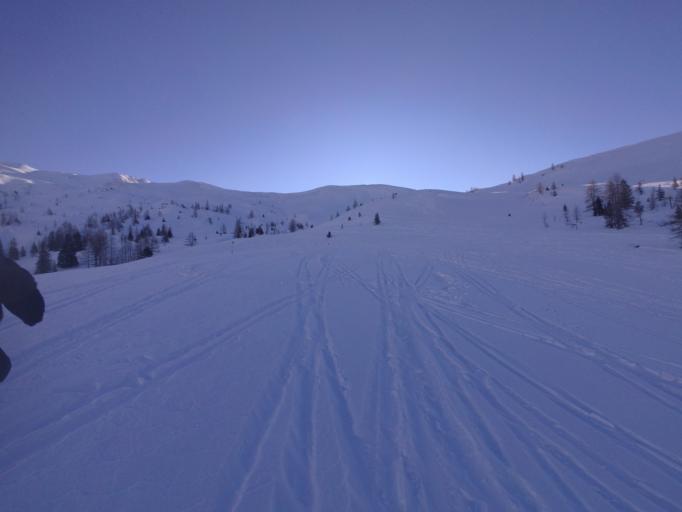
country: AT
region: Salzburg
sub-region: Politischer Bezirk Sankt Johann im Pongau
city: Huttschlag
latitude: 47.1790
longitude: 13.2951
